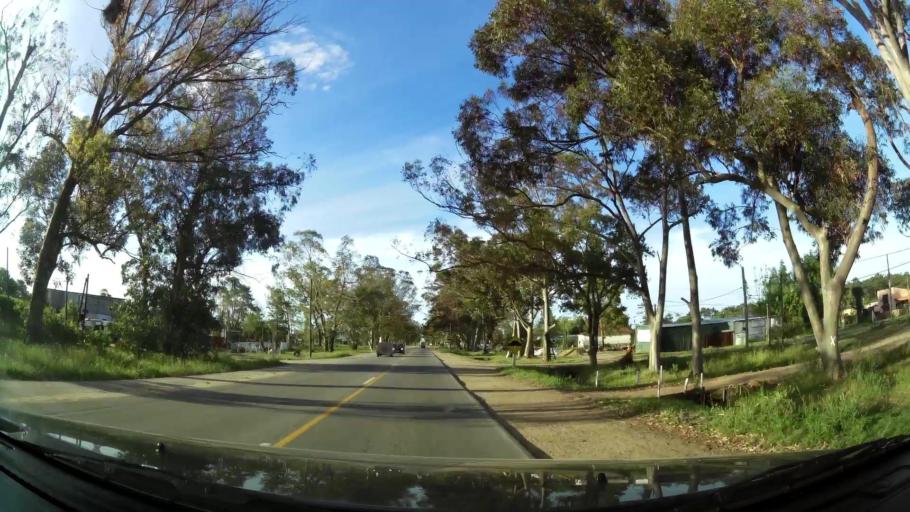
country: UY
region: Canelones
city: Atlantida
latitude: -34.7701
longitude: -55.8415
